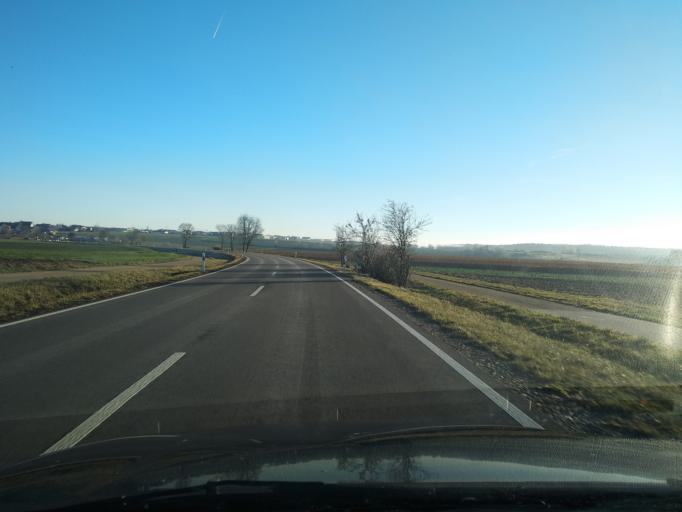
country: DE
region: Baden-Wuerttemberg
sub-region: Regierungsbezirk Stuttgart
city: Deckenpfronn
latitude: 48.6561
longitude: 8.8071
